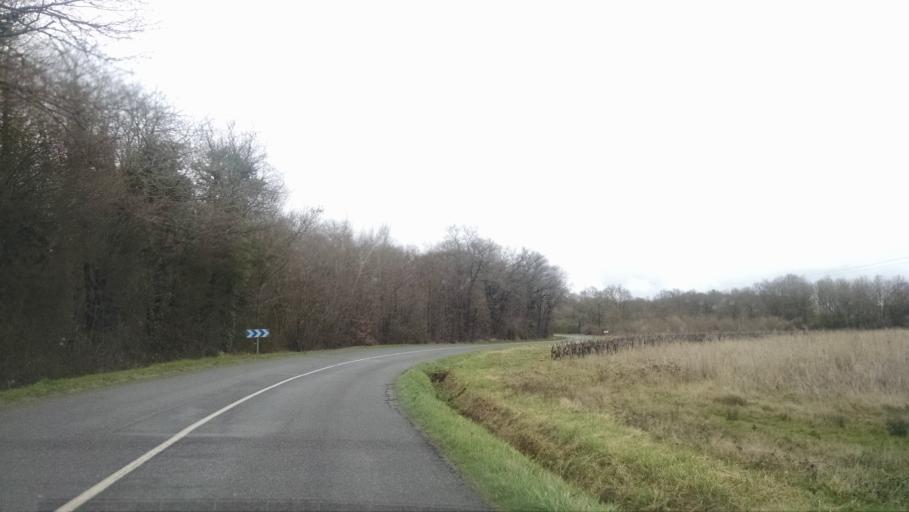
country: FR
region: Pays de la Loire
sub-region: Departement de la Loire-Atlantique
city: Maisdon-sur-Sevre
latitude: 47.1136
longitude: -1.3699
